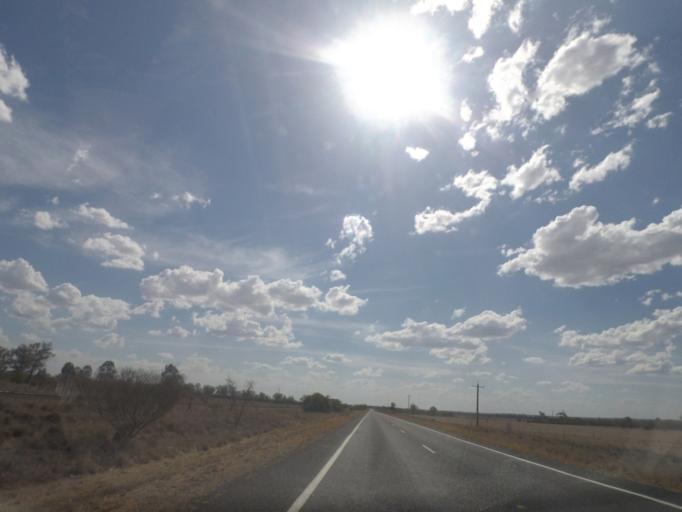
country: AU
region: New South Wales
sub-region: Moree Plains
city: Boggabilla
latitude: -28.4147
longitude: 151.1419
